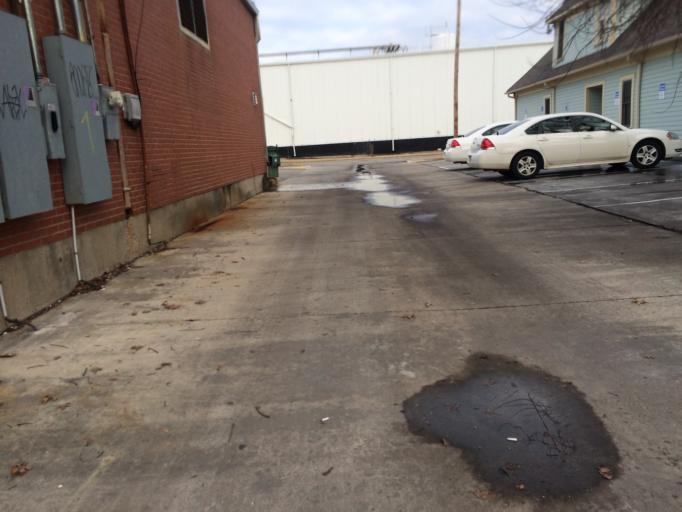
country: US
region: Oklahoma
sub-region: Cleveland County
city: Norman
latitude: 35.2196
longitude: -97.4395
